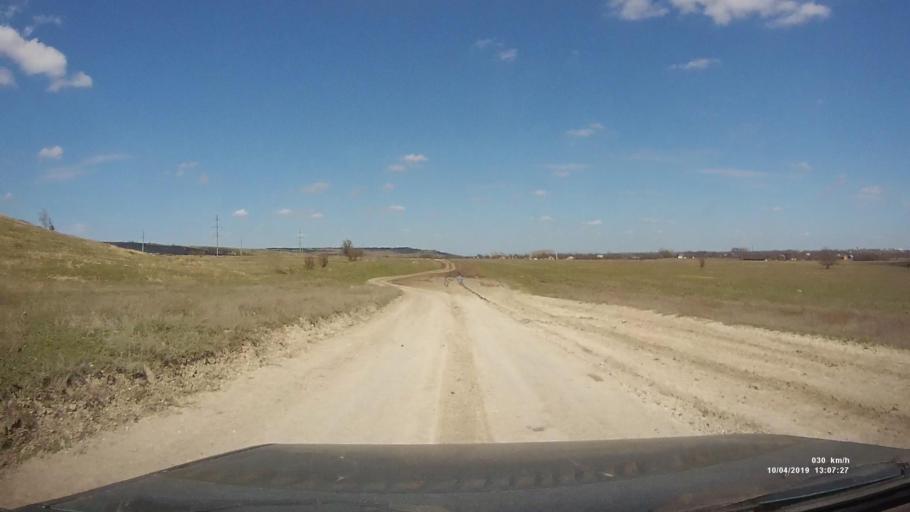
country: RU
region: Rostov
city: Masalovka
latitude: 48.3961
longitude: 40.2406
